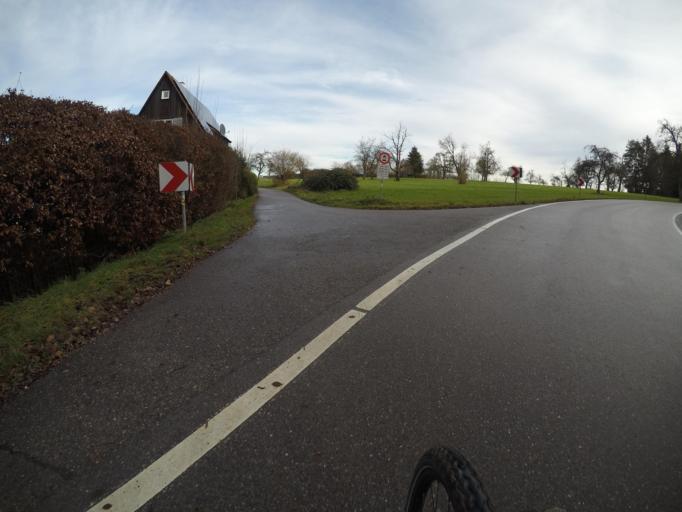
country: DE
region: Baden-Wuerttemberg
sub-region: Regierungsbezirk Stuttgart
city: Baltmannsweiler
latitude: 48.7539
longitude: 9.4364
